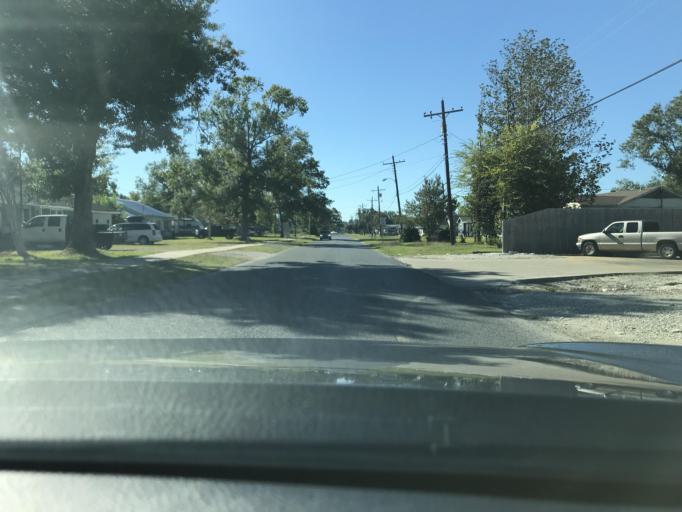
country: US
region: Louisiana
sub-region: Calcasieu Parish
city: Westlake
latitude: 30.2568
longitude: -93.2588
